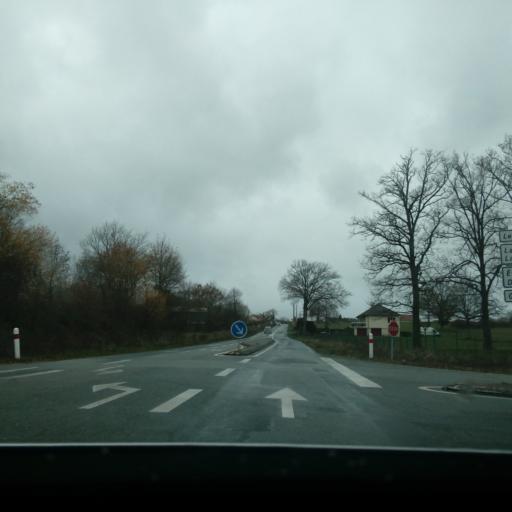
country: FR
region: Limousin
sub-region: Departement de la Creuse
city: Sainte-Feyre
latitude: 46.1757
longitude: 1.9063
